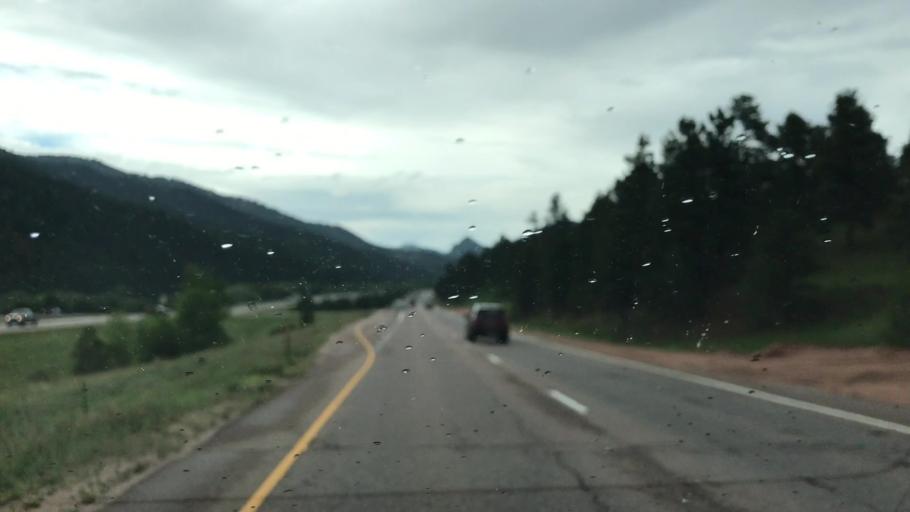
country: US
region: Colorado
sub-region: El Paso County
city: Cascade-Chipita Park
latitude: 38.9412
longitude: -105.0150
